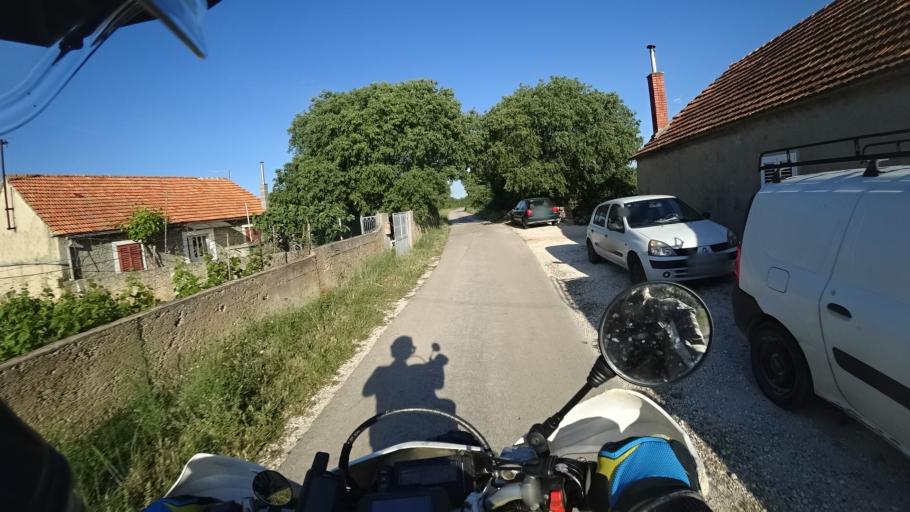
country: HR
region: Sibensko-Kniniska
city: Drnis
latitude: 43.8444
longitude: 16.0368
